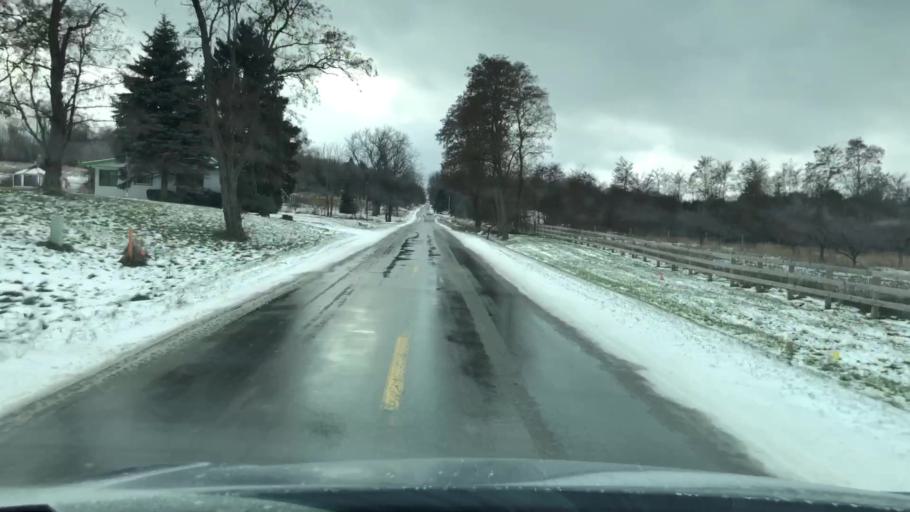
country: US
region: Michigan
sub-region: Antrim County
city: Elk Rapids
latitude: 44.9029
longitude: -85.5154
